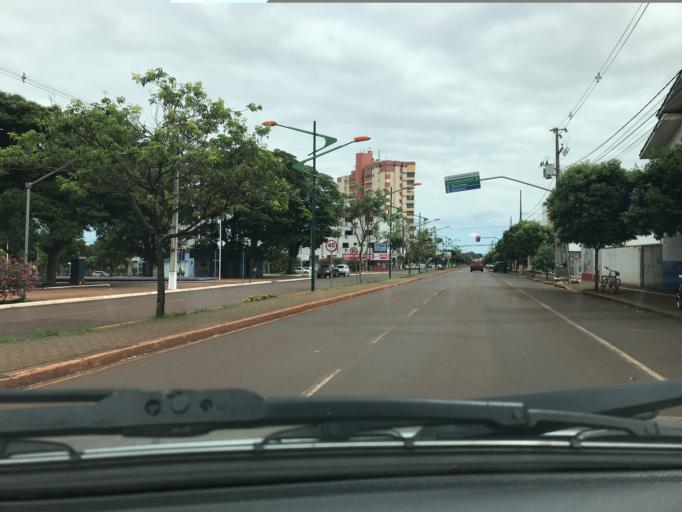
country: BR
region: Parana
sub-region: Palotina
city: Palotina
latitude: -24.2842
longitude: -53.8396
